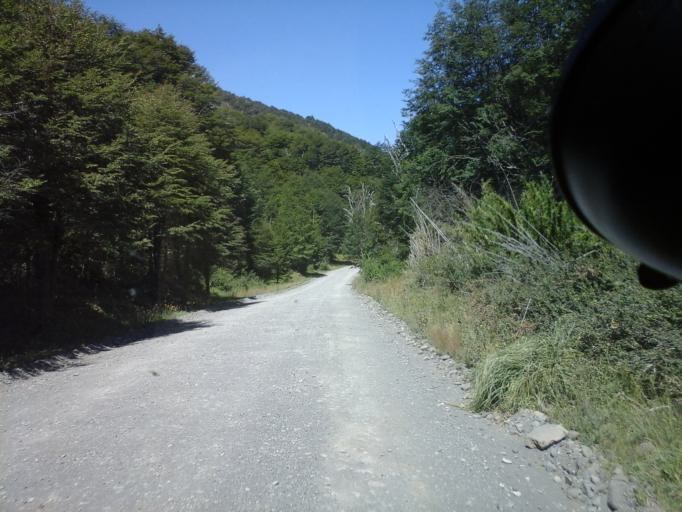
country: AR
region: Neuquen
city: Villa La Angostura
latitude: -41.2145
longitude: -71.8022
